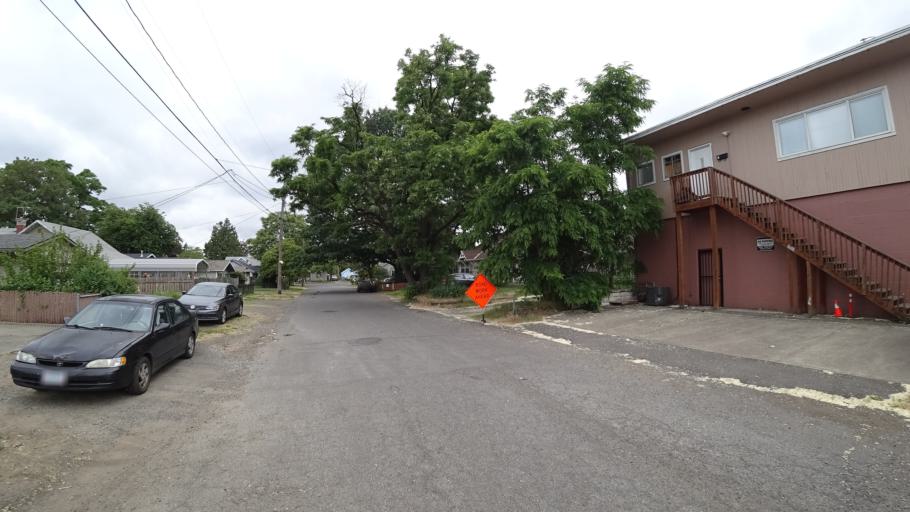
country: US
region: Oregon
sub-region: Multnomah County
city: Lents
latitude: 45.4760
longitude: -122.5802
